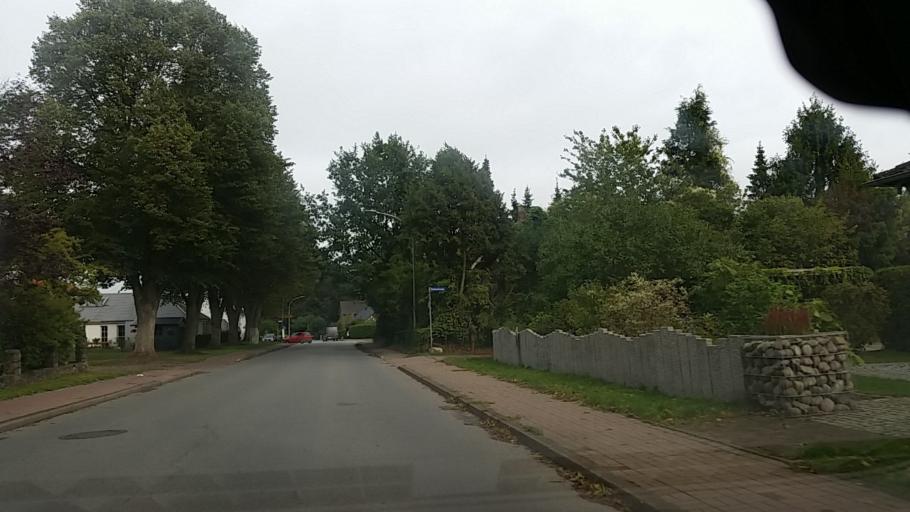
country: DE
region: Schleswig-Holstein
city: Schmalfeld
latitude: 53.8753
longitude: 9.9851
